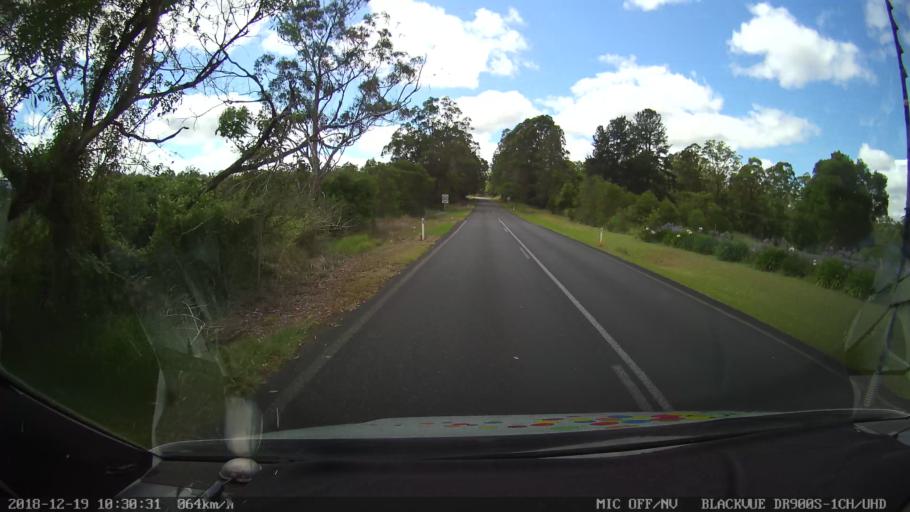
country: AU
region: New South Wales
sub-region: Lismore Municipality
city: Larnook
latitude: -28.5894
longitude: 153.1082
